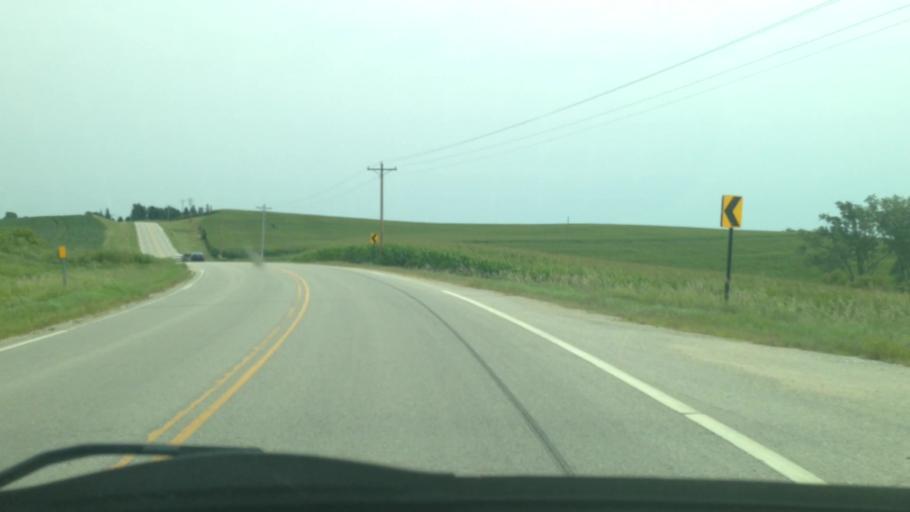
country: US
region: Minnesota
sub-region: Fillmore County
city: Preston
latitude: 43.7278
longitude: -91.9975
